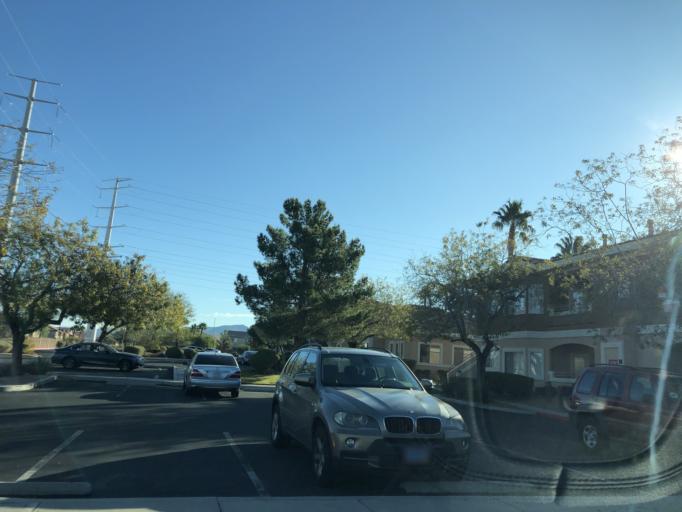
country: US
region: Nevada
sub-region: Clark County
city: Whitney
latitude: 36.0022
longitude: -115.0918
